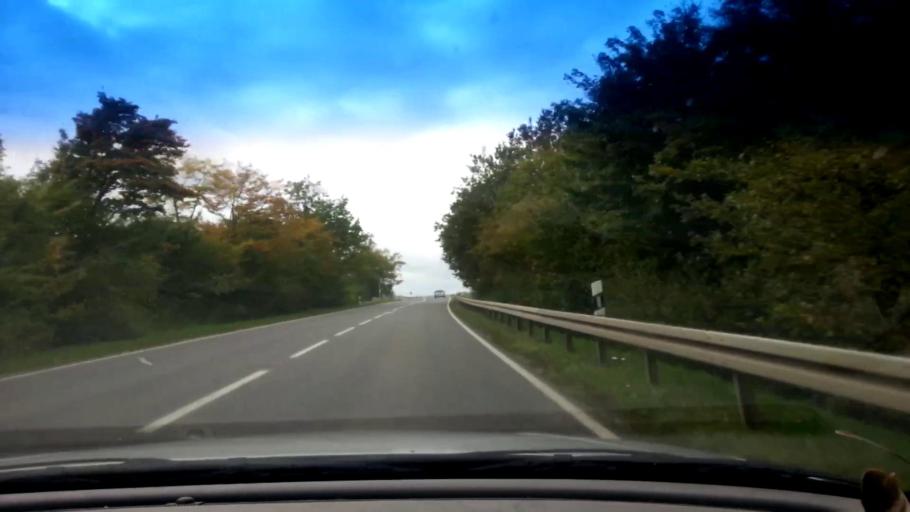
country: DE
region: Bavaria
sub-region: Upper Franconia
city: Viereth-Trunstadt
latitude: 49.9029
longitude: 10.7869
